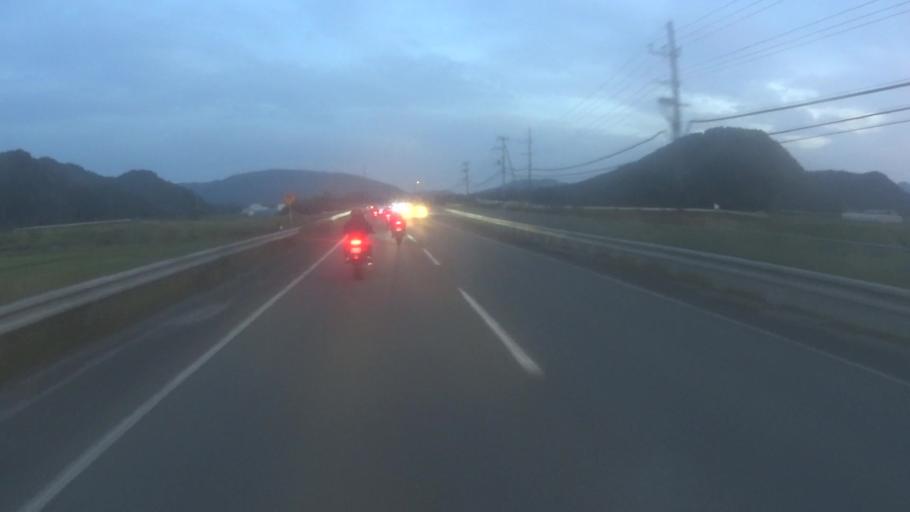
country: JP
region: Kyoto
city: Ayabe
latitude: 35.1864
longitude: 135.4173
